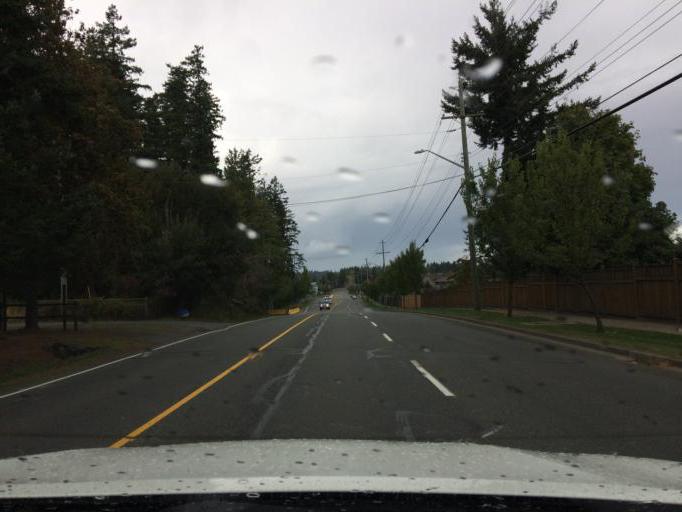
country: CA
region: British Columbia
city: Courtenay
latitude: 49.6924
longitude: -124.9502
